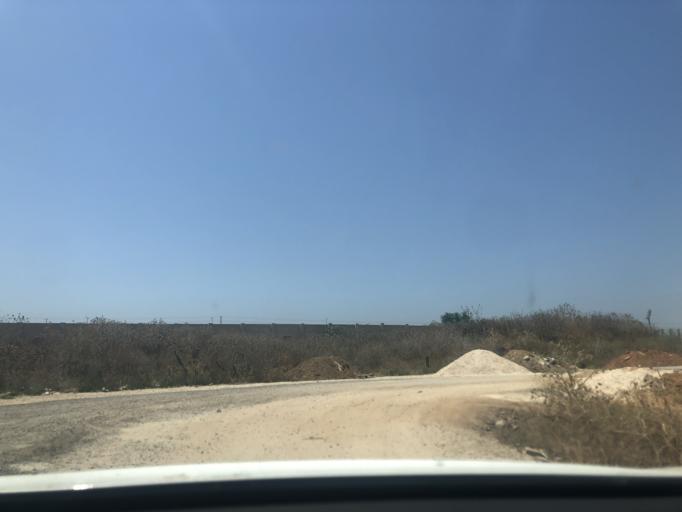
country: IL
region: Central District
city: Lod
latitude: 31.9351
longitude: 34.8947
